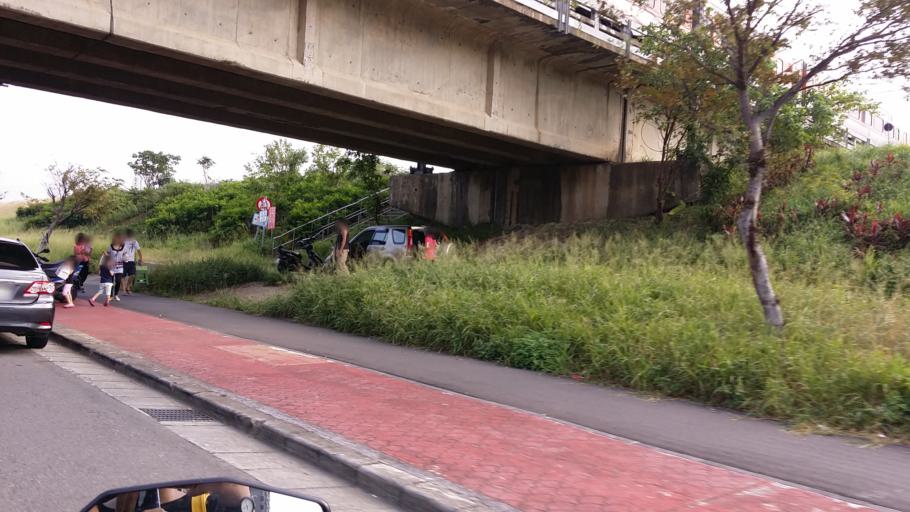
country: TW
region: Taiwan
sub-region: Hsinchu
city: Zhubei
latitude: 24.8246
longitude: 120.9996
